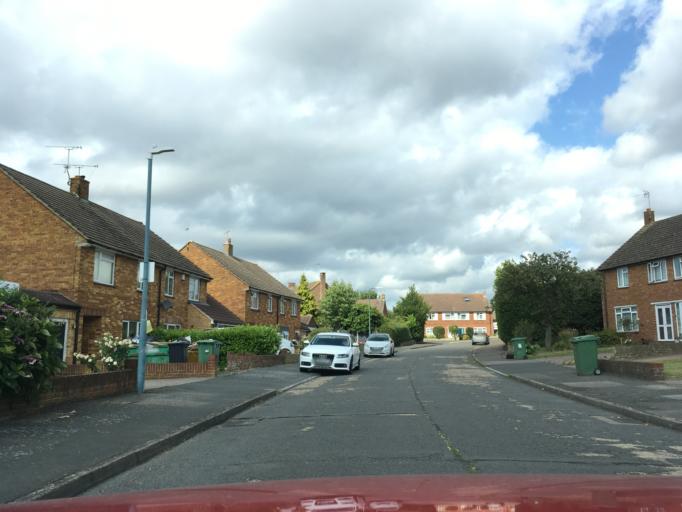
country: GB
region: England
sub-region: Kent
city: Maidstone
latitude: 51.2503
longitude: 0.5207
